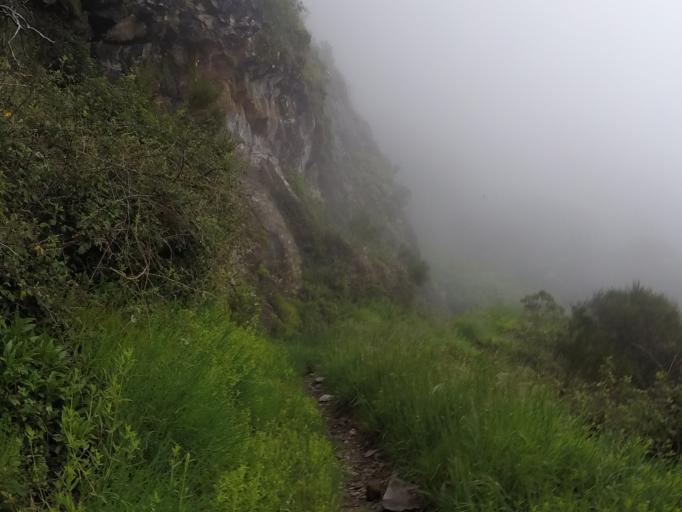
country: PT
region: Madeira
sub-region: Camara de Lobos
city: Curral das Freiras
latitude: 32.7334
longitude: -16.9876
